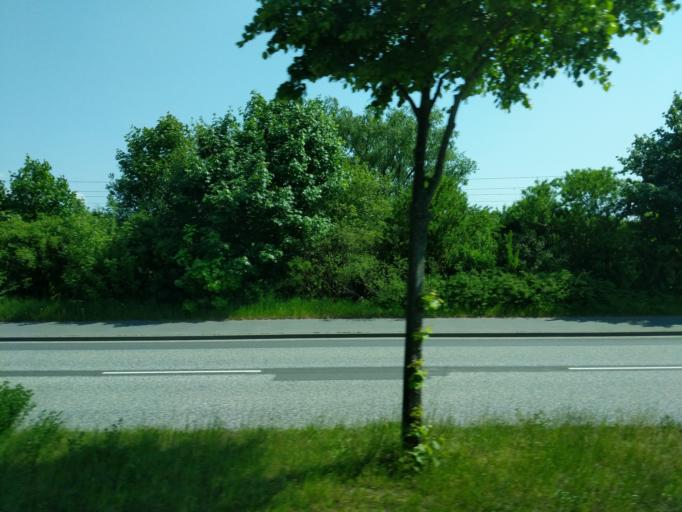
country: DE
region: Mecklenburg-Vorpommern
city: Feldstadt
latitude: 53.5769
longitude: 11.3973
